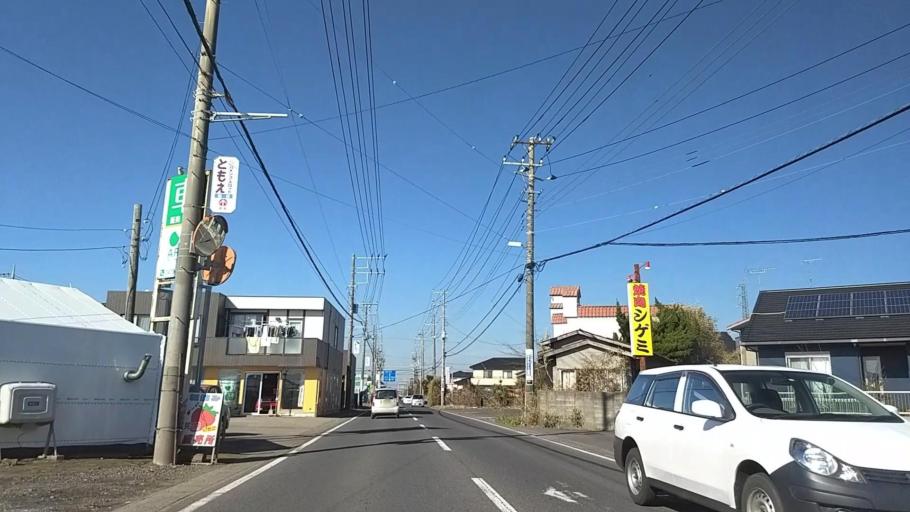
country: JP
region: Chiba
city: Asahi
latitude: 35.7200
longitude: 140.6783
